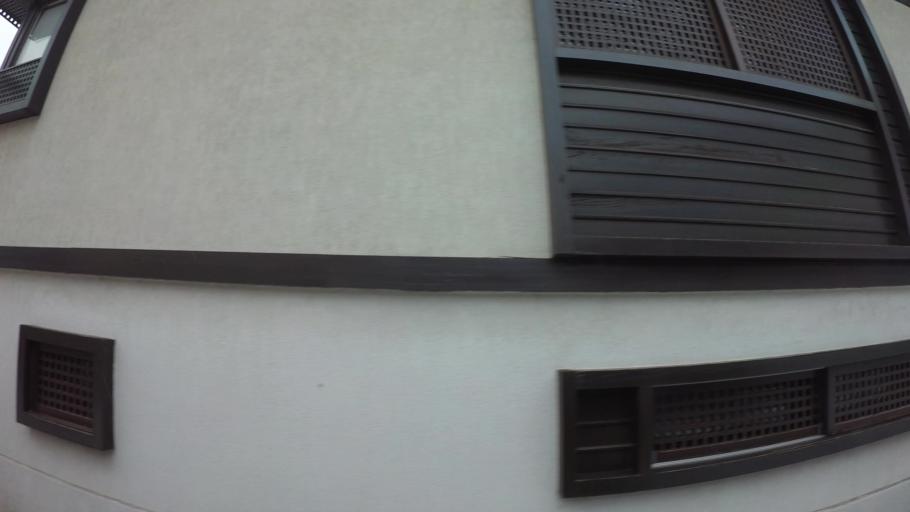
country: BA
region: Federation of Bosnia and Herzegovina
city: Kobilja Glava
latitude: 43.8638
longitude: 18.4348
